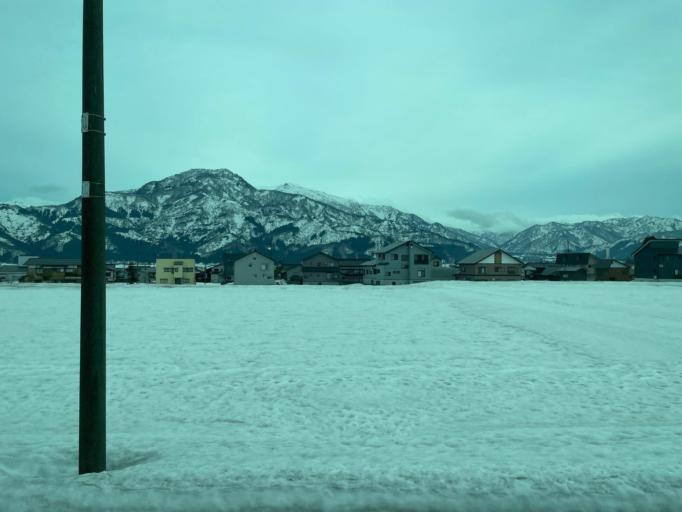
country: JP
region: Niigata
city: Shiozawa
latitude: 37.0496
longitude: 138.8619
